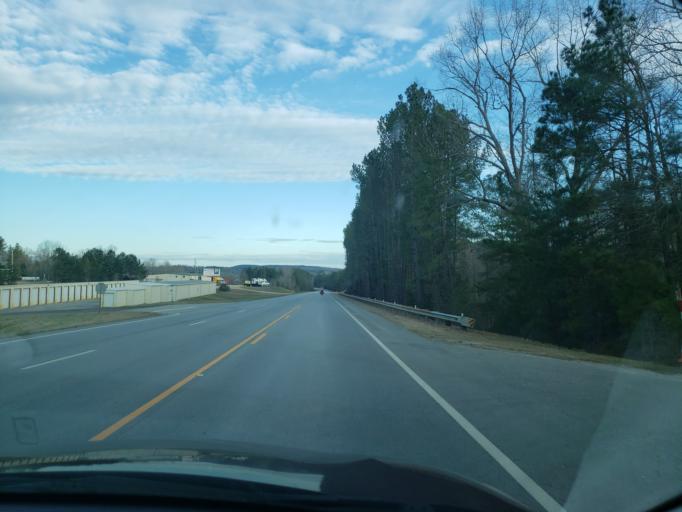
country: US
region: Alabama
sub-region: Randolph County
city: Wedowee
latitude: 33.3564
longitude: -85.4903
